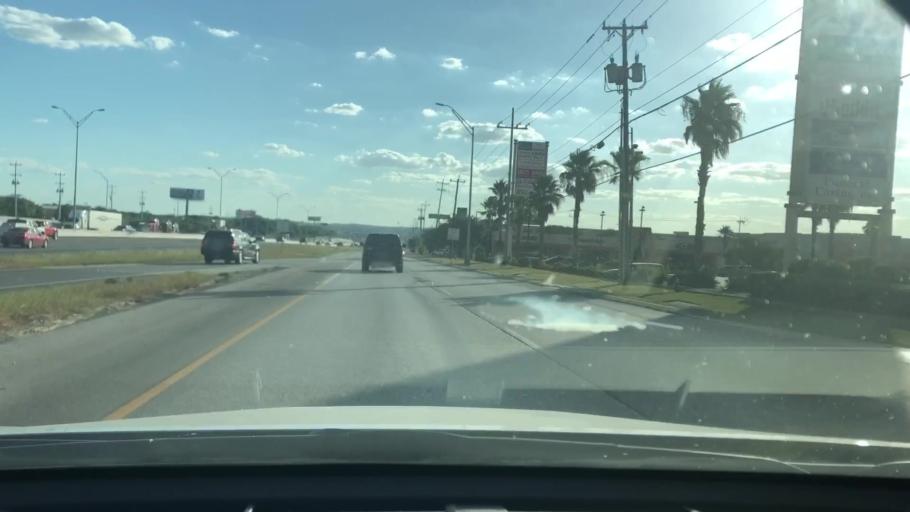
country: US
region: Texas
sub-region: Bexar County
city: Selma
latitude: 29.5984
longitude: -98.2804
